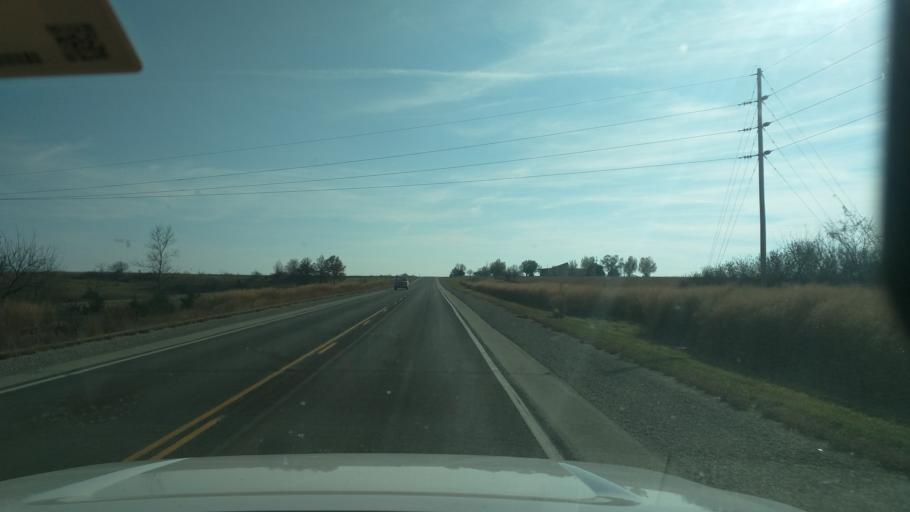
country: US
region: Kansas
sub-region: Lyon County
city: Emporia
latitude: 38.3365
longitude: -96.1803
